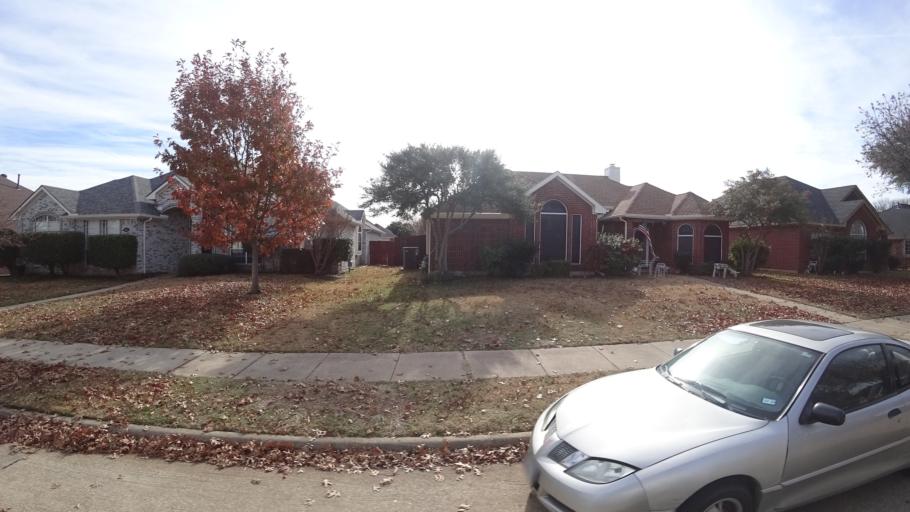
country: US
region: Texas
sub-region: Denton County
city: Highland Village
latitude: 33.0647
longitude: -97.0432
